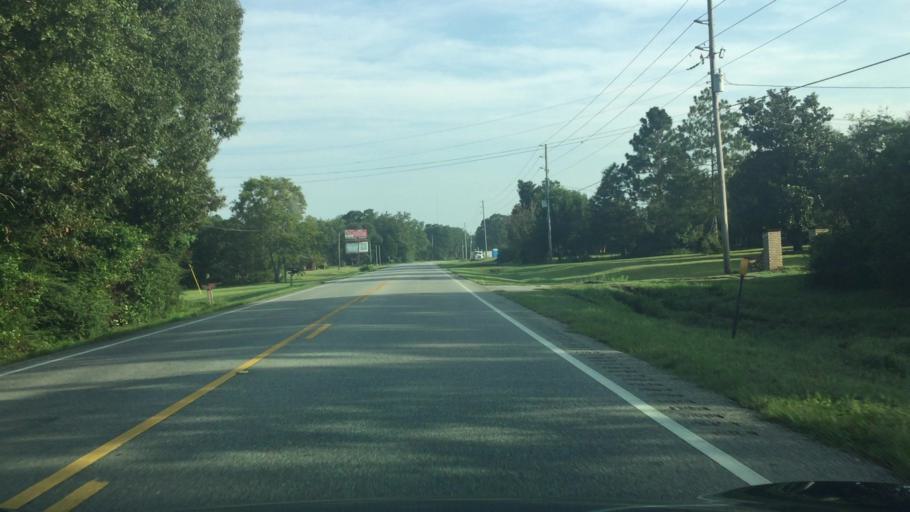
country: US
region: Alabama
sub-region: Covington County
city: Andalusia
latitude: 31.2666
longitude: -86.4729
